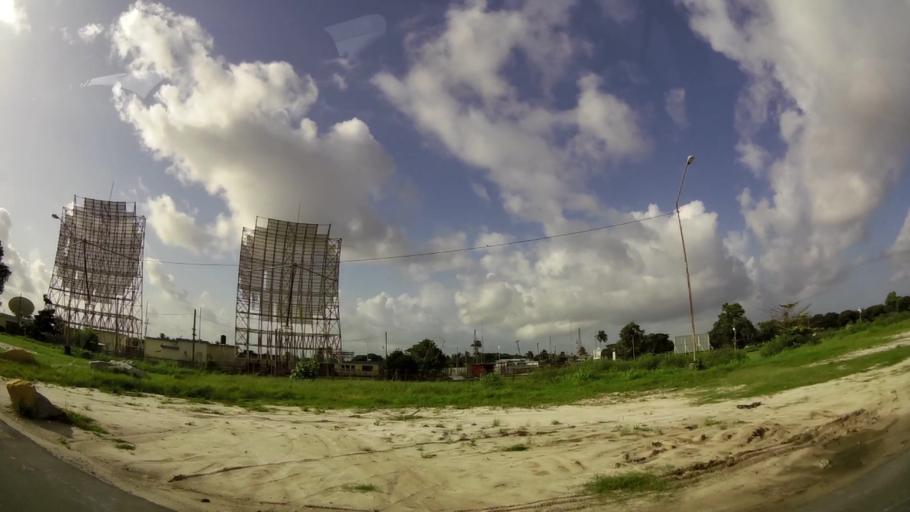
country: GY
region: Demerara-Mahaica
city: Georgetown
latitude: 6.8253
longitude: -58.1478
